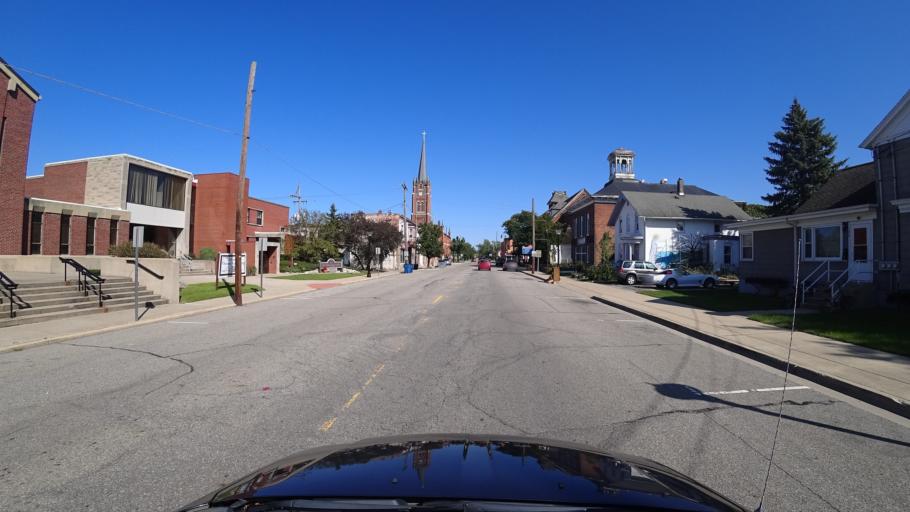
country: US
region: Indiana
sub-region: LaPorte County
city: Michigan City
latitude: 41.7125
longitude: -86.9009
